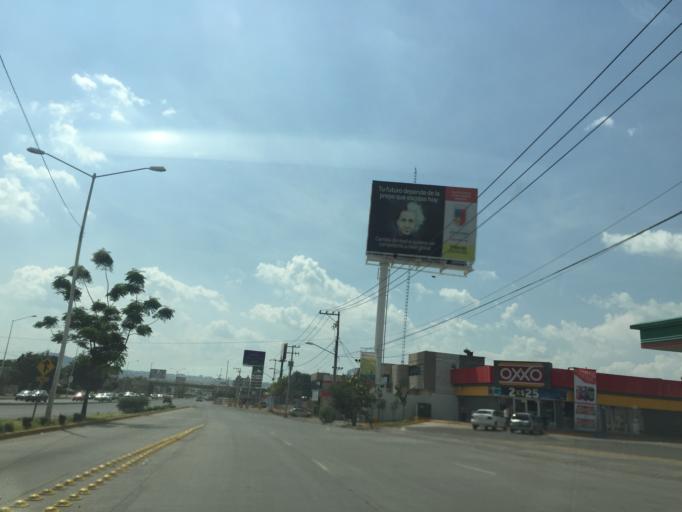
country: MX
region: Guanajuato
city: Leon
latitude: 21.1735
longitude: -101.6611
